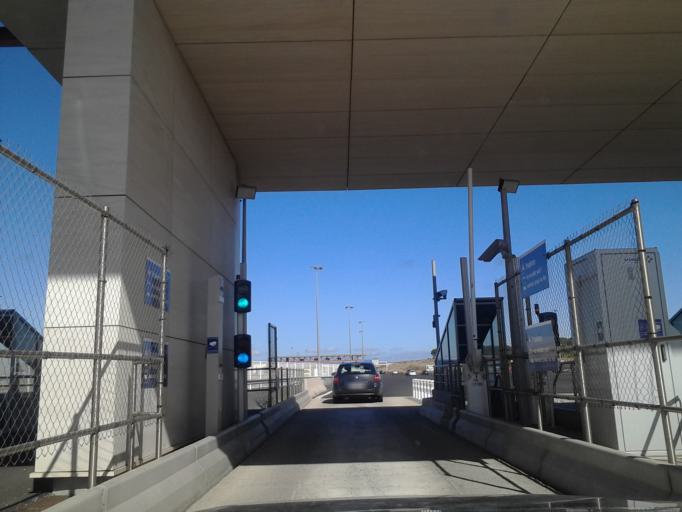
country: FR
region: Languedoc-Roussillon
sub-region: Departement de l'Herault
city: Cers
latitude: 43.3431
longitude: 3.2890
